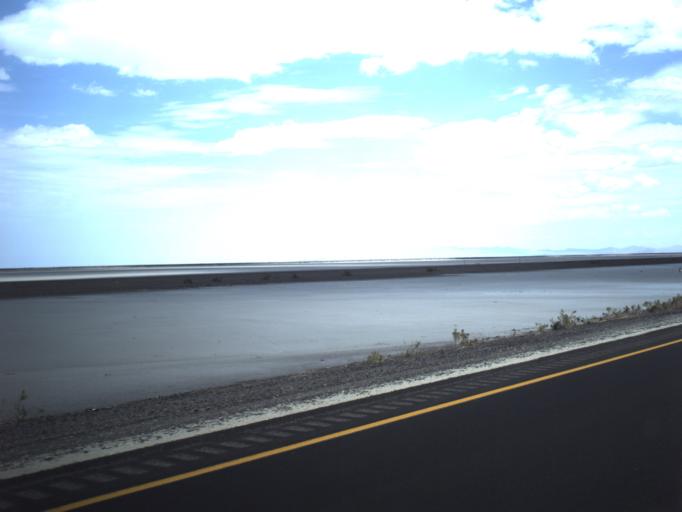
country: US
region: Utah
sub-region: Tooele County
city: Wendover
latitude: 40.7322
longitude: -113.5592
